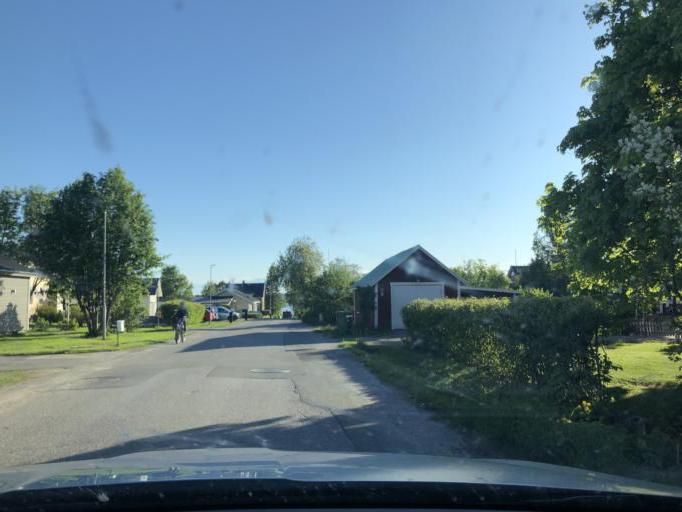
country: SE
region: Norrbotten
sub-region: Lulea Kommun
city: Sodra Sunderbyn
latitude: 65.6583
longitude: 21.9367
